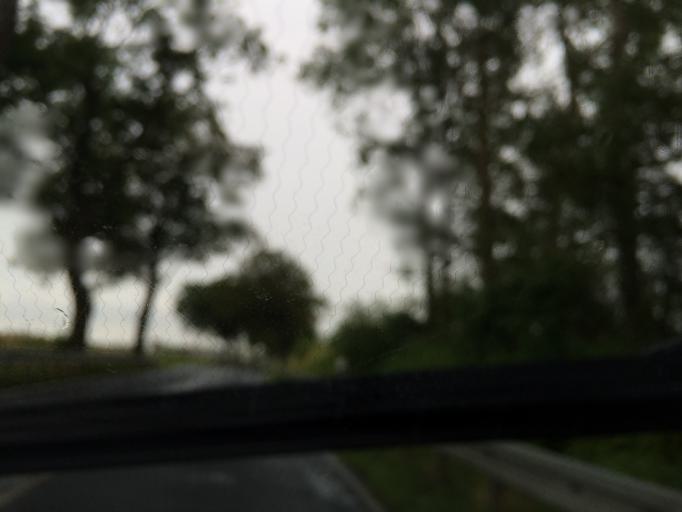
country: DE
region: Mecklenburg-Vorpommern
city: Kramerhof
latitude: 54.3567
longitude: 13.0382
